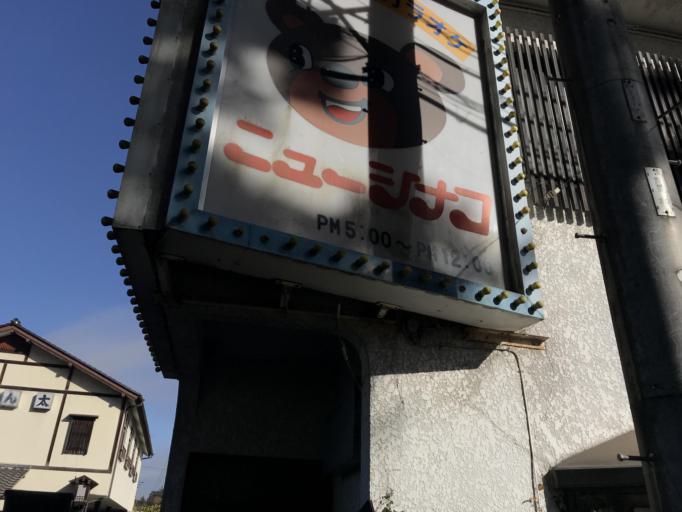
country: JP
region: Tochigi
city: Kanuma
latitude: 36.5848
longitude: 139.7499
